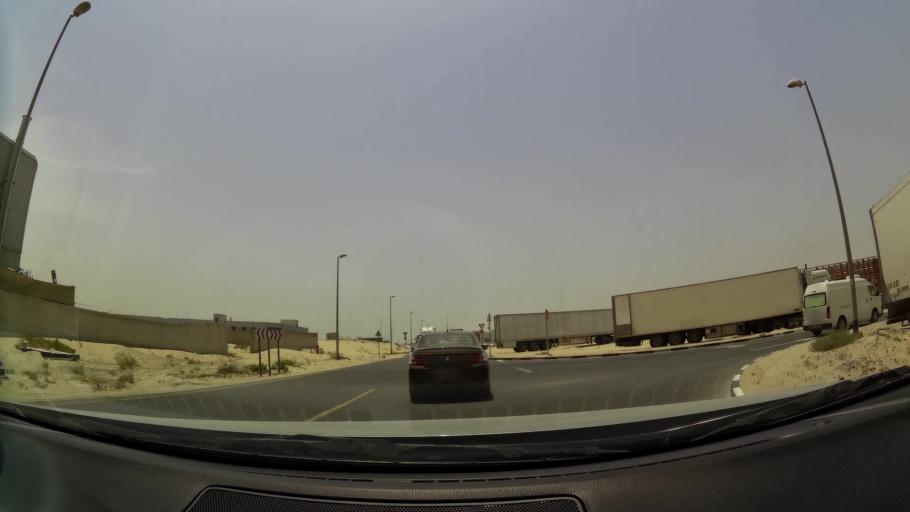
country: AE
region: Ash Shariqah
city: Sharjah
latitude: 25.1856
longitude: 55.3794
